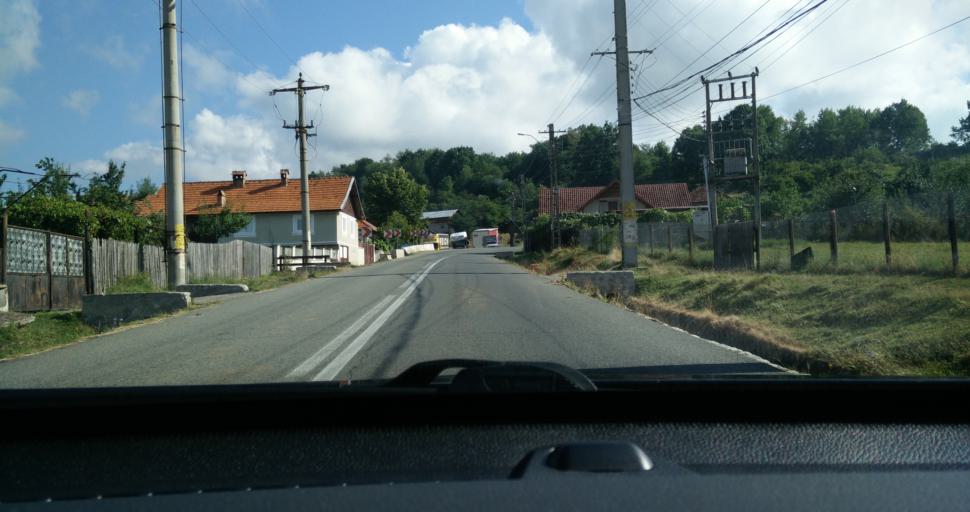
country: RO
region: Gorj
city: Novaci-Straini
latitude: 45.1819
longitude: 23.6775
